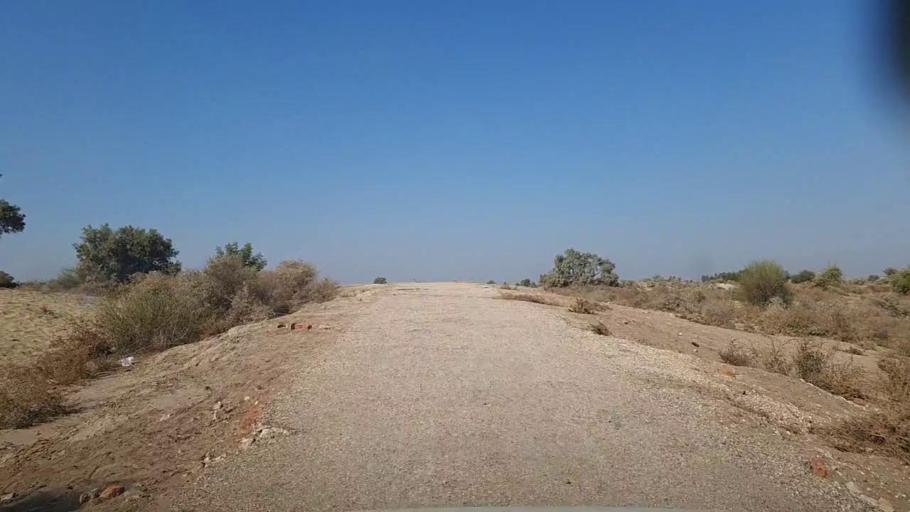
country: PK
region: Sindh
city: Khairpur
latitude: 27.9555
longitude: 69.7334
